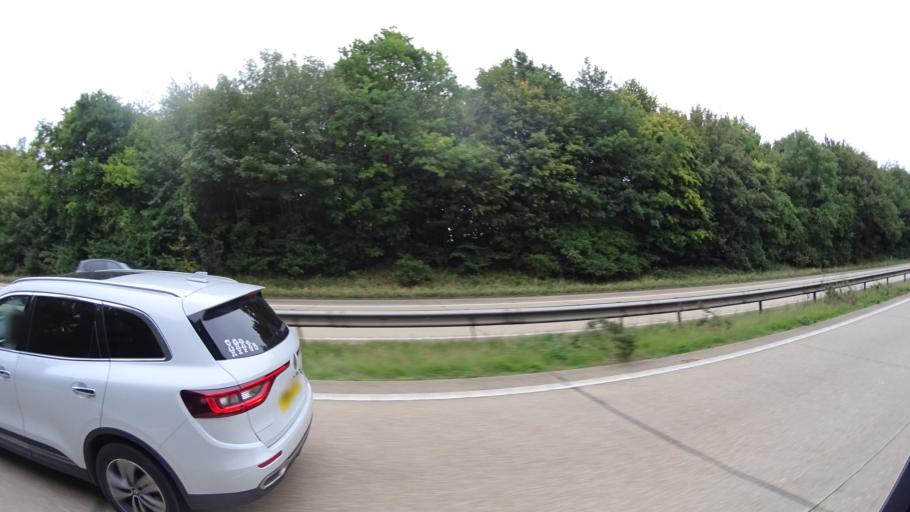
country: GB
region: England
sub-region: Hampshire
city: Overton
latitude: 51.1633
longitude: -1.2322
